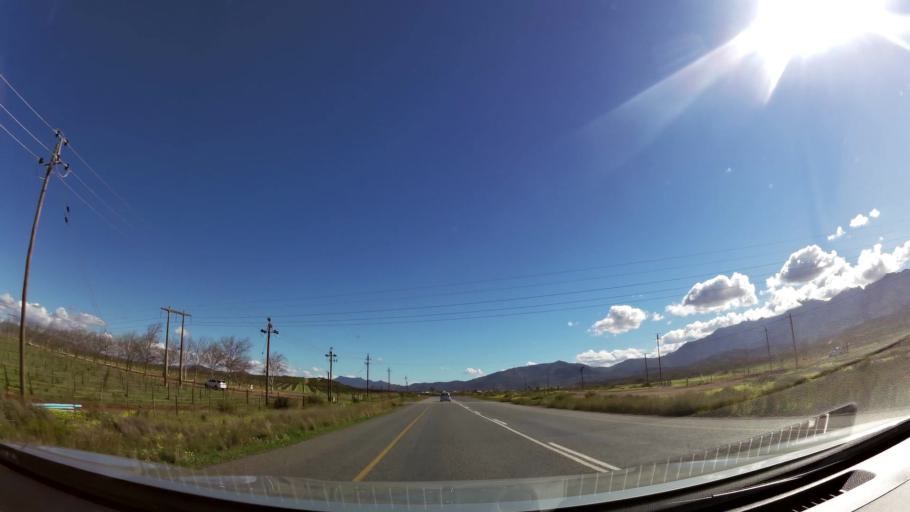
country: ZA
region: Western Cape
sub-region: Cape Winelands District Municipality
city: Ashton
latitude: -33.8151
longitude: 19.9394
